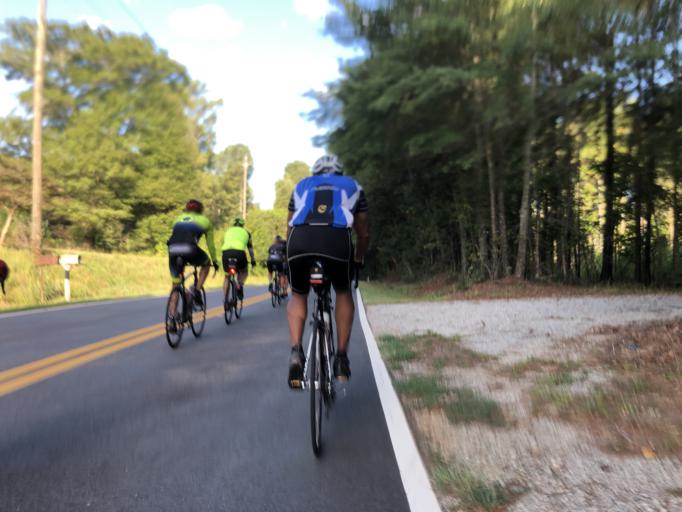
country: US
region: Georgia
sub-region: Fulton County
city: Palmetto
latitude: 33.5811
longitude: -84.6931
